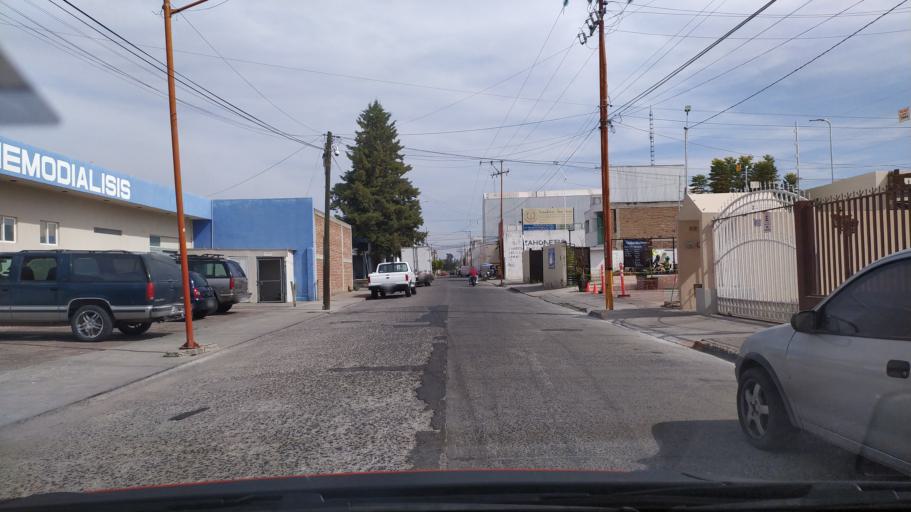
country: MX
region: Guanajuato
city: San Francisco del Rincon
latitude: 21.0244
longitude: -101.8528
